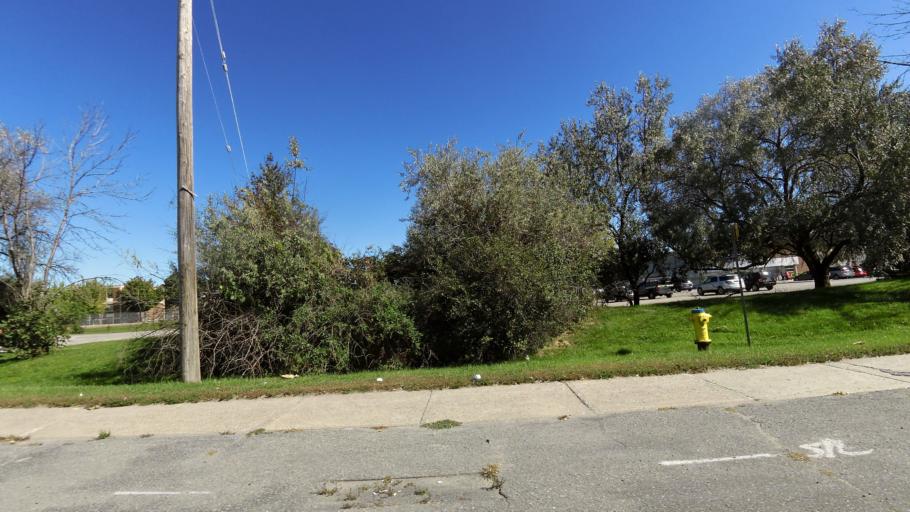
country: CA
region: Ontario
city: Ottawa
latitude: 45.3420
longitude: -75.7282
